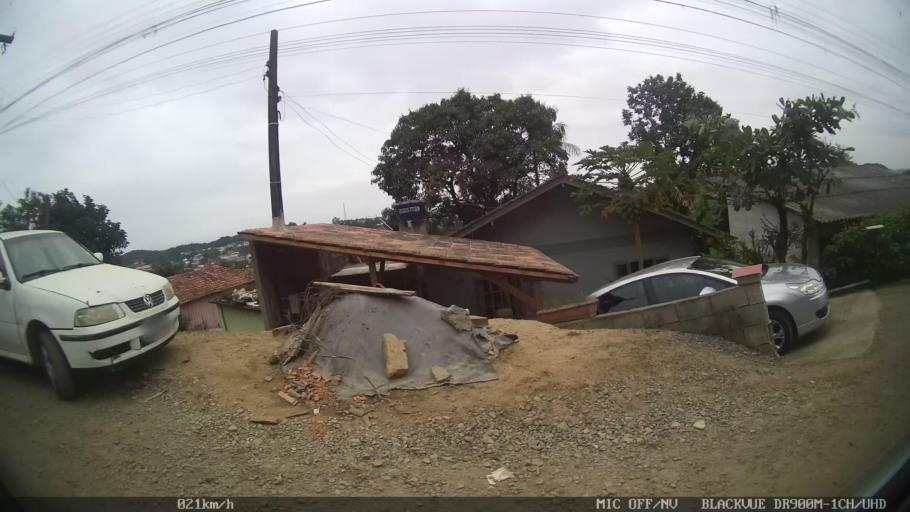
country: BR
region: Santa Catarina
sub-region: Joinville
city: Joinville
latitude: -26.3502
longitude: -48.8274
